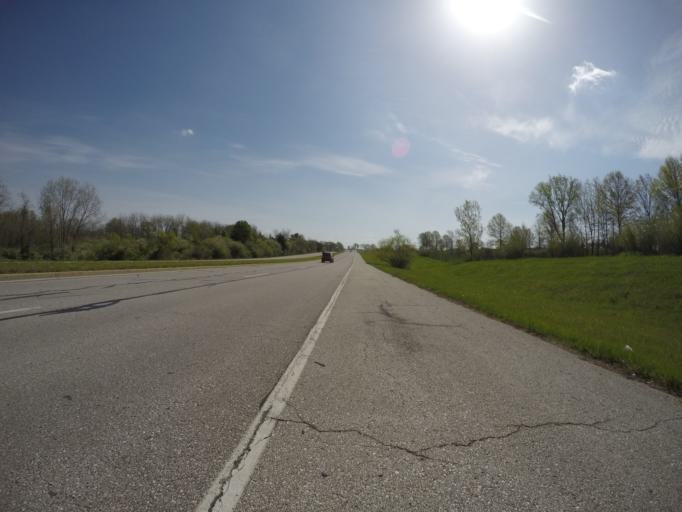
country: US
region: Missouri
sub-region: Jackson County
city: Lees Summit
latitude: 38.9240
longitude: -94.4587
